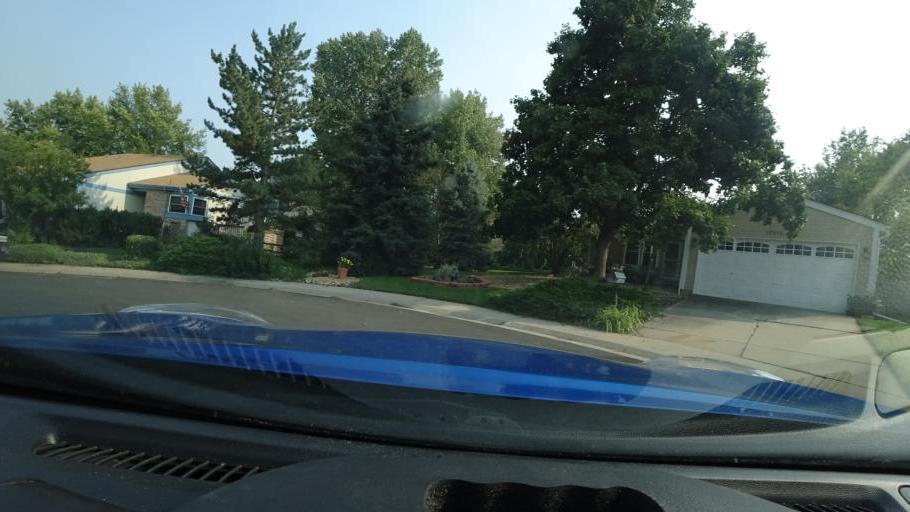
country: US
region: Colorado
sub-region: Adams County
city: Aurora
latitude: 39.6655
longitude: -104.7798
